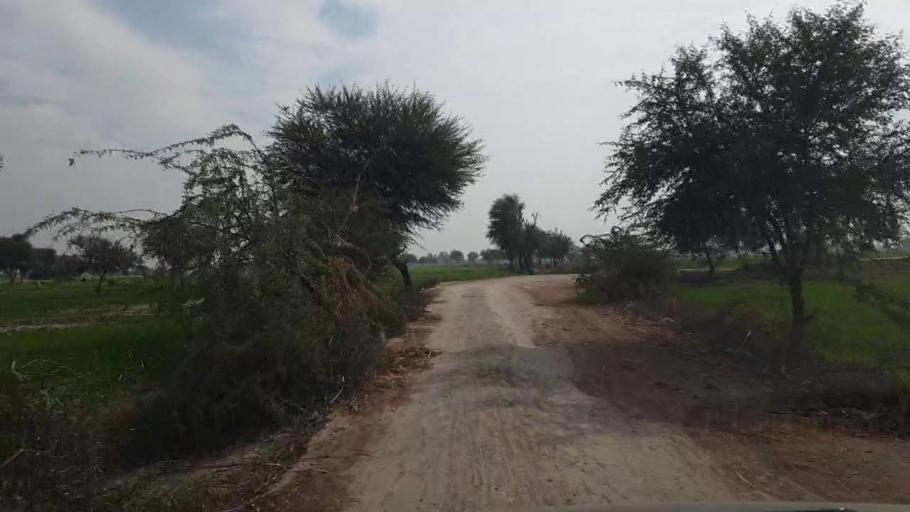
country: PK
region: Sindh
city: Shahdadpur
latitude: 25.9545
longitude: 68.6979
